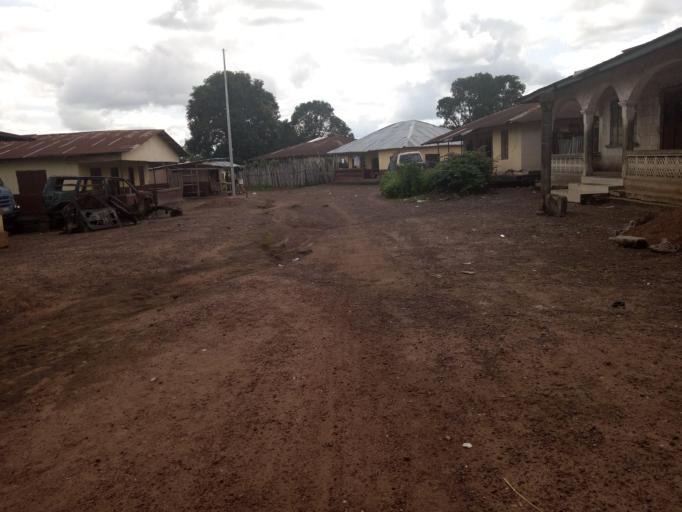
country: SL
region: Northern Province
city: Kamakwie
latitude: 9.4951
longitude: -12.2426
